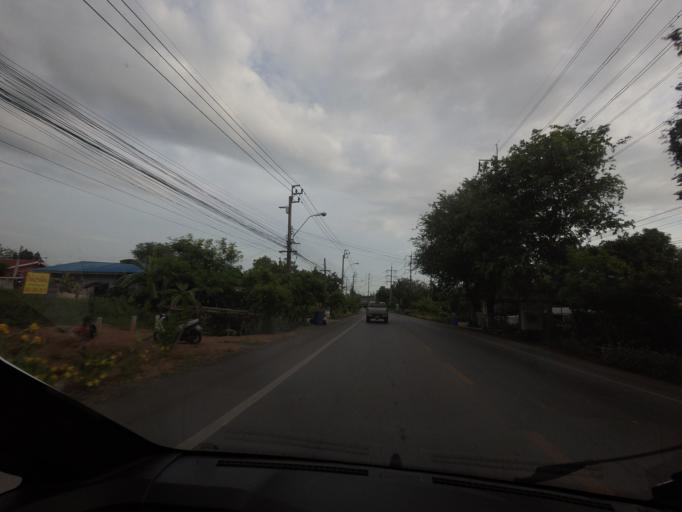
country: TH
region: Bangkok
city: Nong Chok
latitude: 13.8633
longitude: 100.8607
